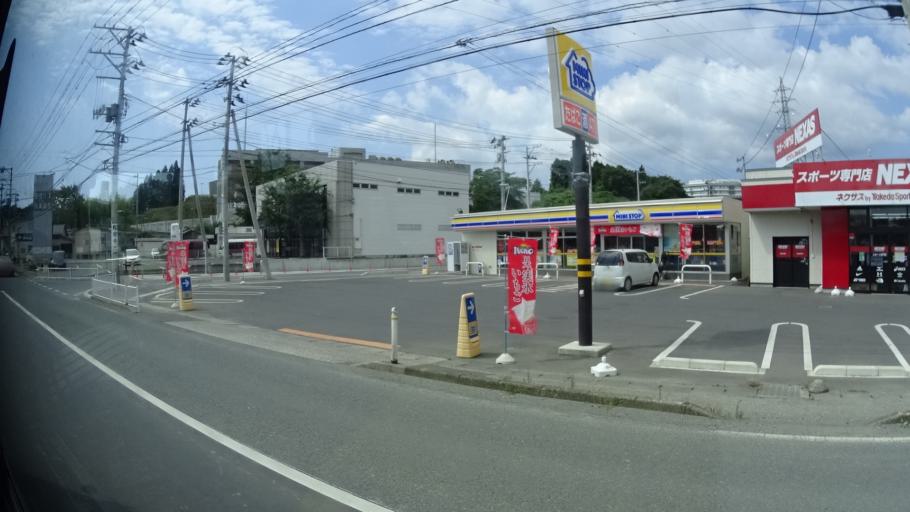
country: JP
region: Iwate
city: Ofunato
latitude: 38.8897
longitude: 141.5704
